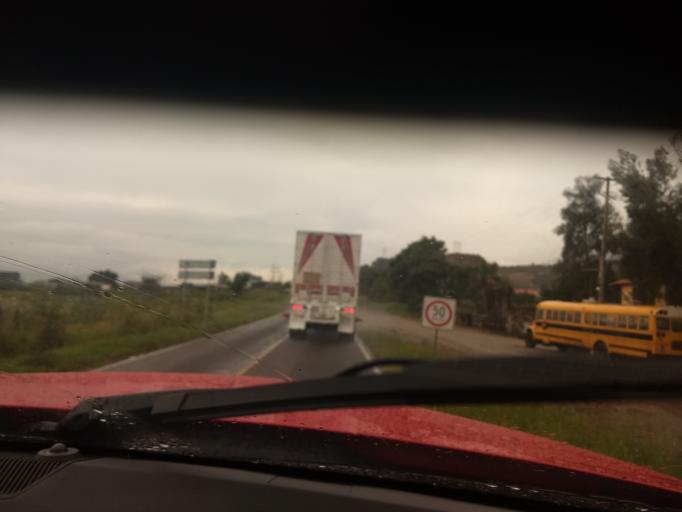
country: MX
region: Jalisco
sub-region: Zapotlan el Grande
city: Ciudad Guzman [CERESO]
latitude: 19.6493
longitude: -103.4728
